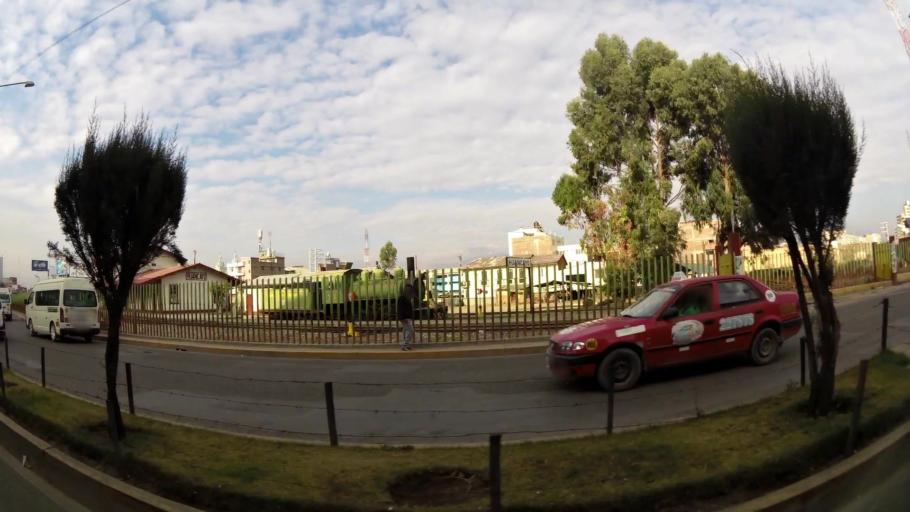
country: PE
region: Junin
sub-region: Provincia de Huancayo
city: Huancayo
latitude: -12.0668
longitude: -75.2059
